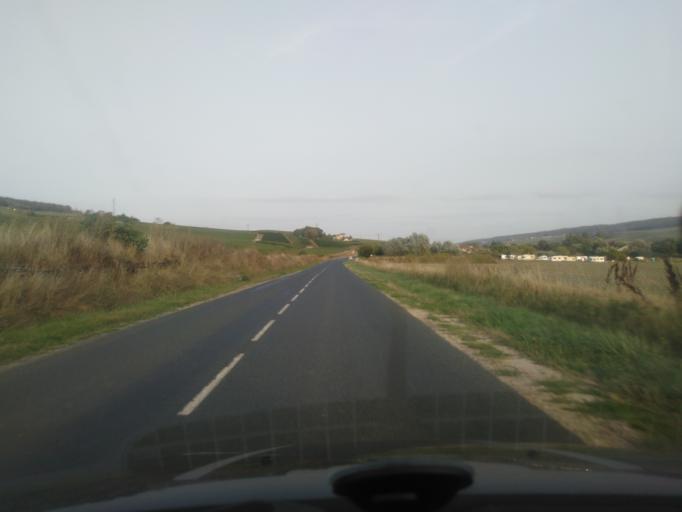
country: FR
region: Champagne-Ardenne
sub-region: Departement de la Marne
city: Mareuil-le-Port
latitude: 49.0866
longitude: 3.7895
